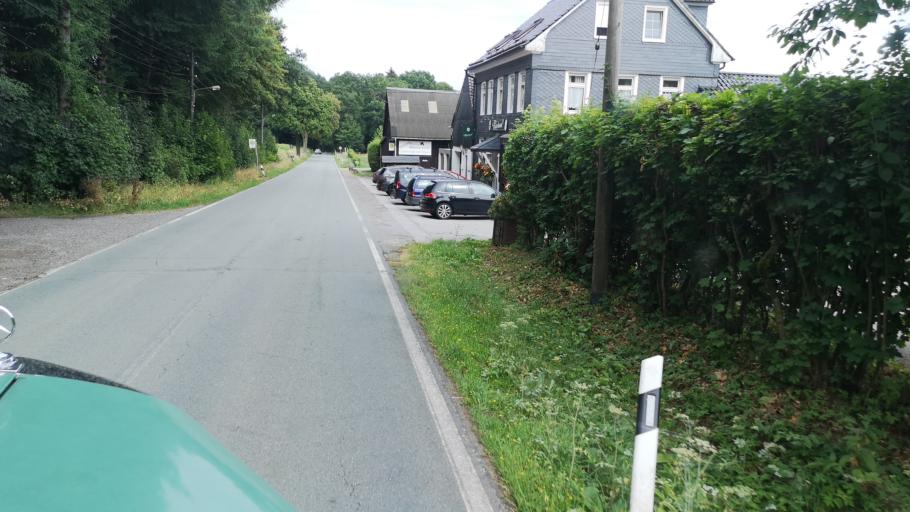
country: DE
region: North Rhine-Westphalia
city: Huckeswagen
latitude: 51.1744
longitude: 7.2901
